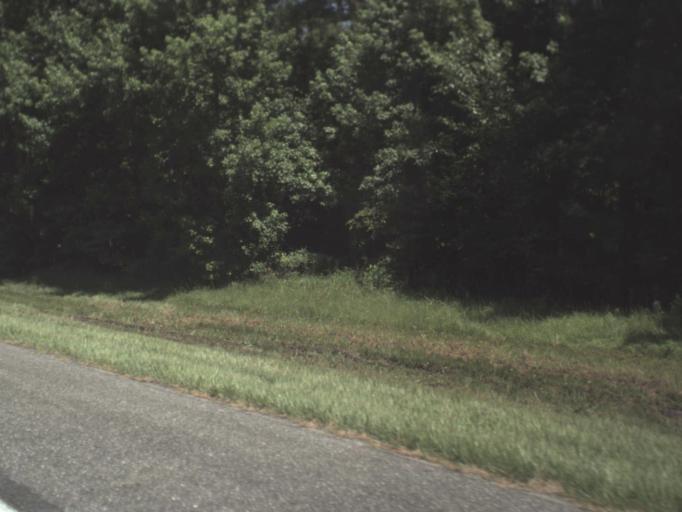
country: US
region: Florida
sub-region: Jefferson County
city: Monticello
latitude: 30.4452
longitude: -83.7042
